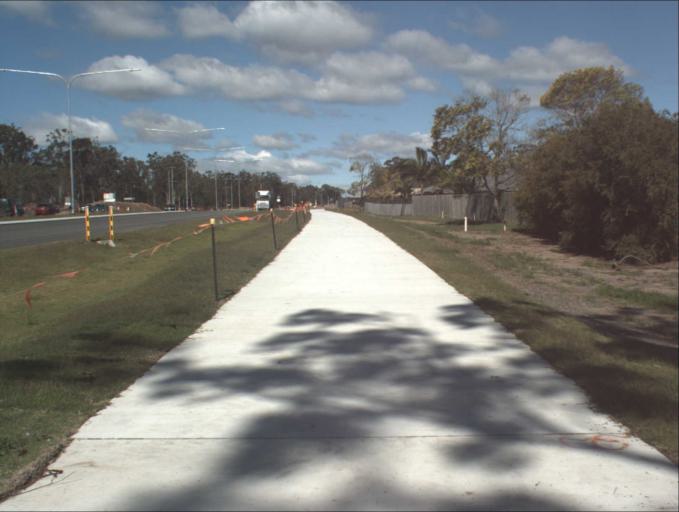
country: AU
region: Queensland
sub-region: Logan
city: Logan Reserve
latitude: -27.6983
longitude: 153.1003
